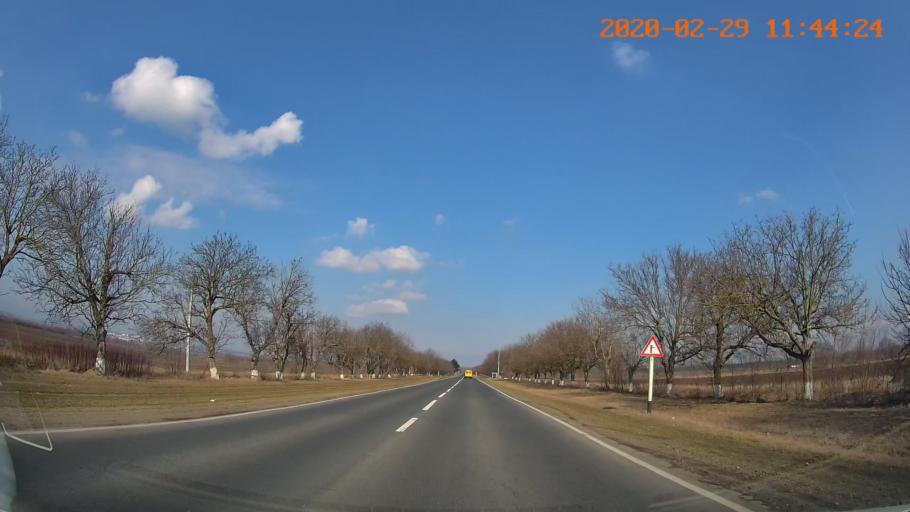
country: MD
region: Rezina
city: Saharna
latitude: 47.7107
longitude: 29.0008
